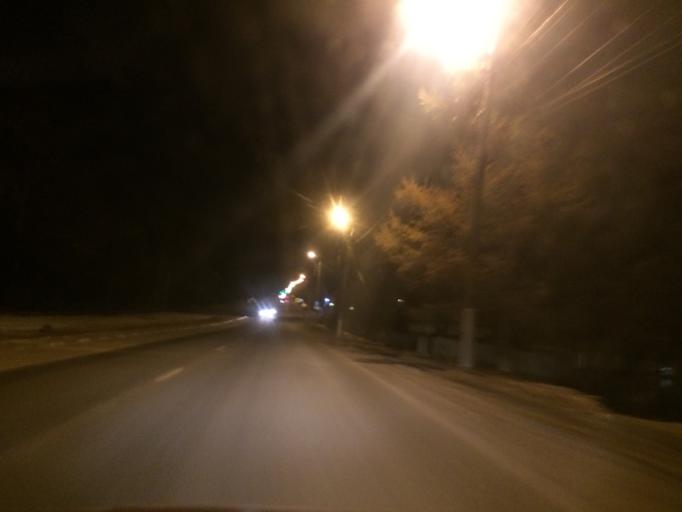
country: RU
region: Tula
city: Tula
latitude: 54.1866
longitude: 37.7030
